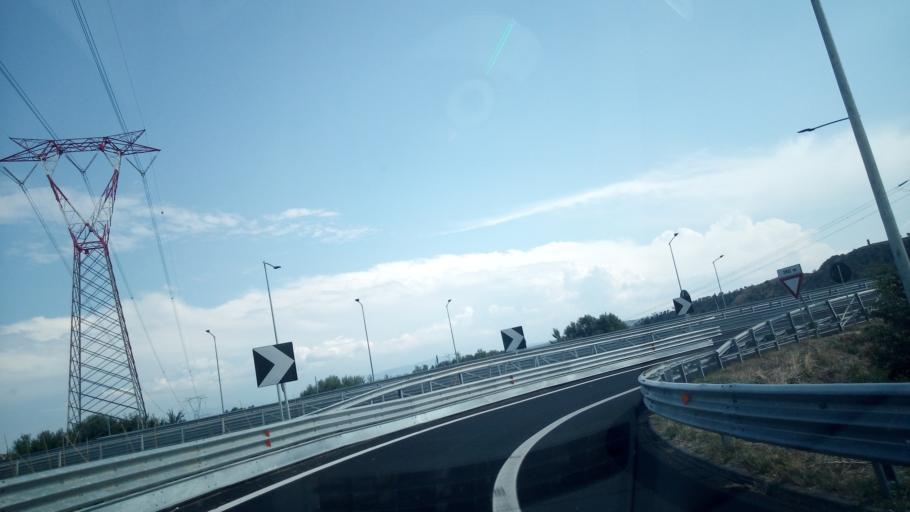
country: IT
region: Calabria
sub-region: Provincia di Cosenza
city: Doria
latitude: 39.7243
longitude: 16.3182
